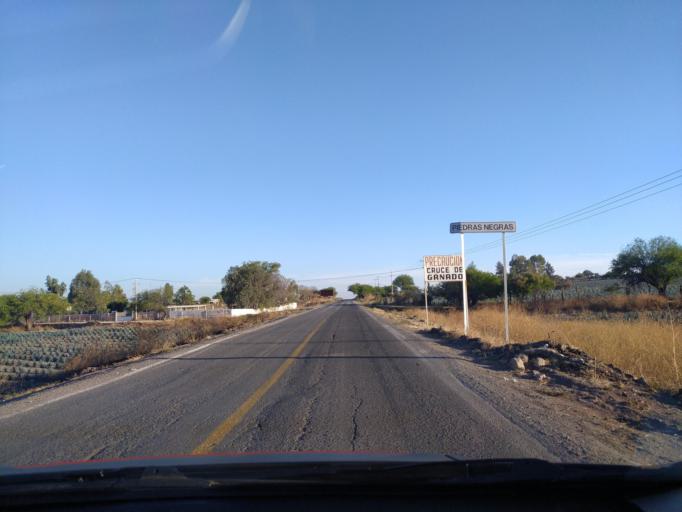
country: MX
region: Guanajuato
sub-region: San Francisco del Rincon
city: San Ignacio de Hidalgo
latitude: 20.8195
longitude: -101.8410
